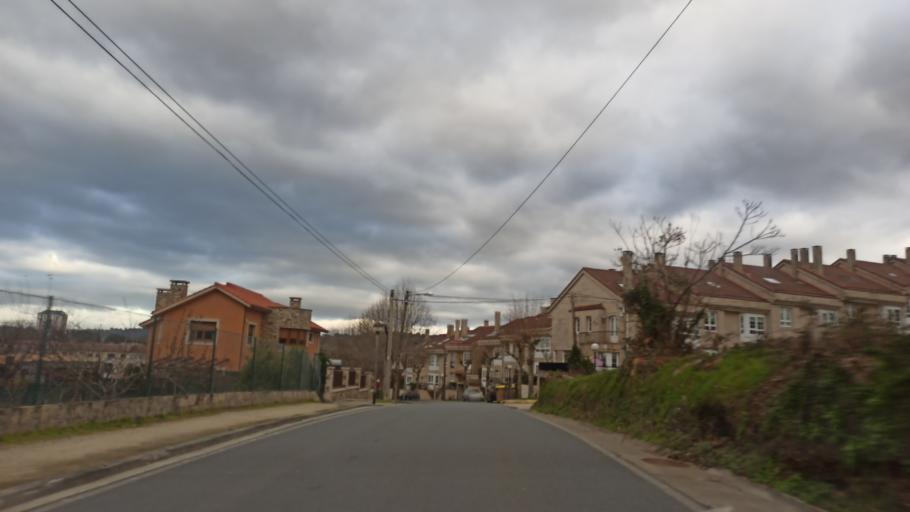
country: ES
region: Galicia
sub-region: Provincia da Coruna
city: Oleiros
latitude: 43.3382
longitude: -8.3506
